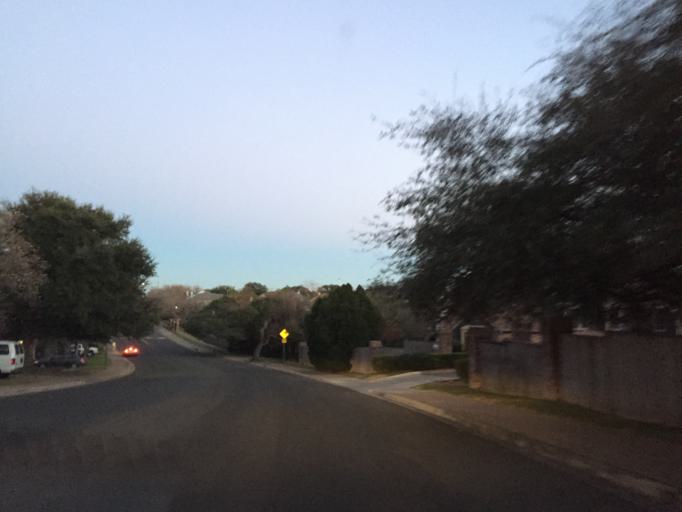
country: US
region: Texas
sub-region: Travis County
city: Wells Branch
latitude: 30.3963
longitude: -97.6957
